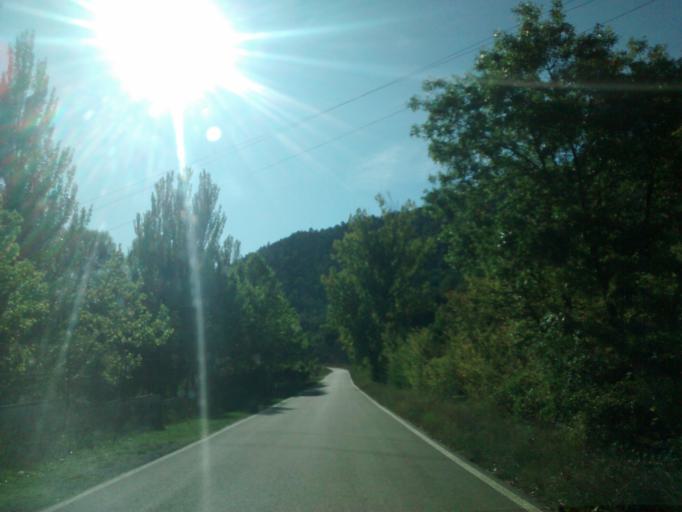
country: ES
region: Aragon
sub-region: Provincia de Huesca
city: Loarre
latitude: 42.4073
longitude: -0.6472
